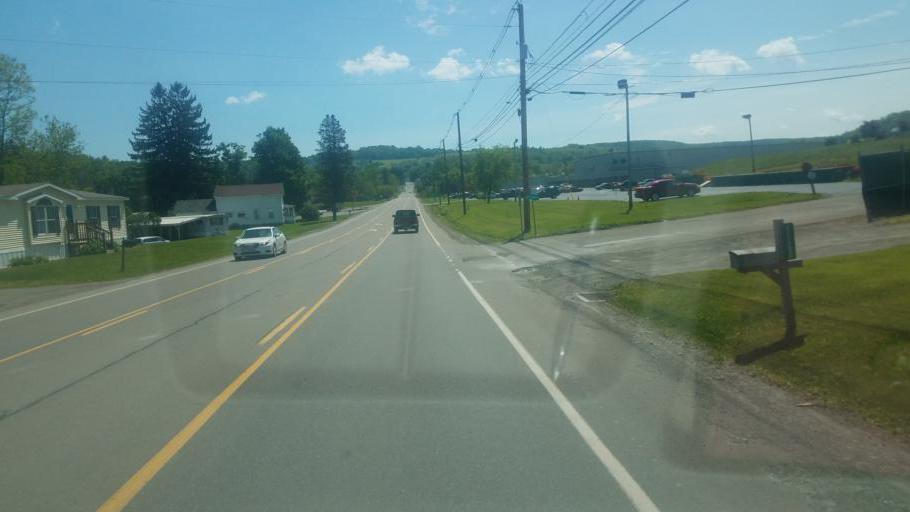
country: US
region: Pennsylvania
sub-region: Tioga County
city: Wellsboro
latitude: 41.7451
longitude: -77.2760
